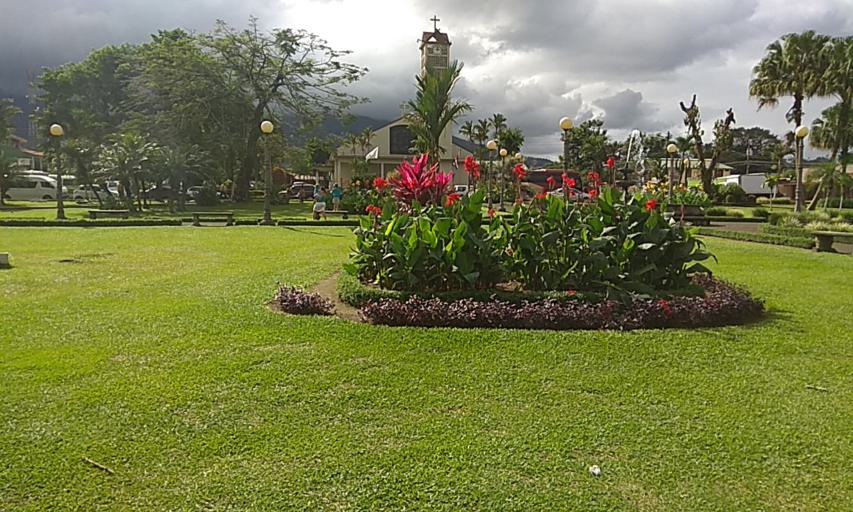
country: CR
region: Alajuela
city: La Fortuna
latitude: 10.4717
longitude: -84.6449
